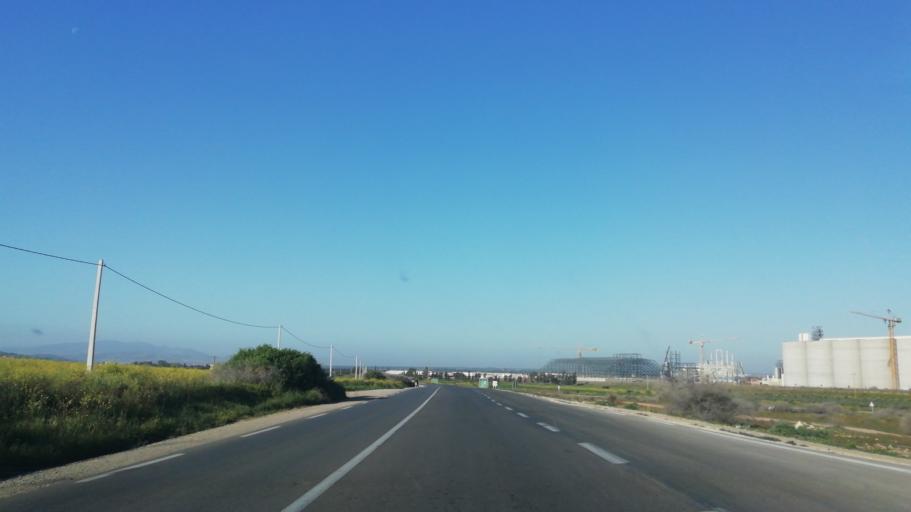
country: DZ
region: Mascara
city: Mascara
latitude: 35.6393
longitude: 0.1432
